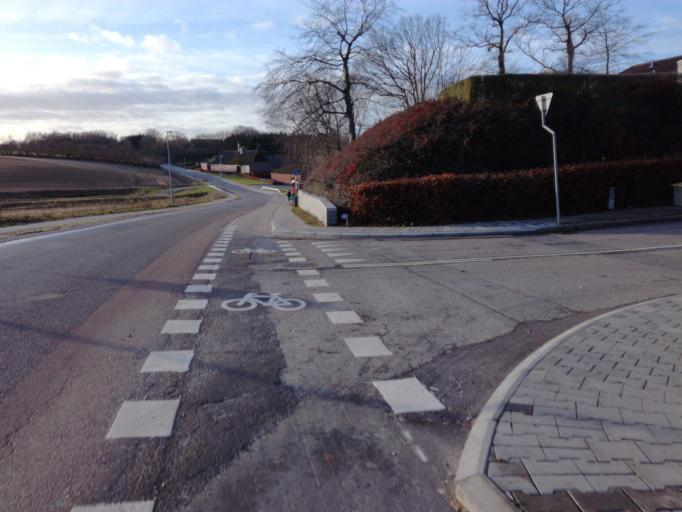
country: DK
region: South Denmark
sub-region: Fredericia Kommune
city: Fredericia
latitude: 55.6177
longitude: 9.7541
